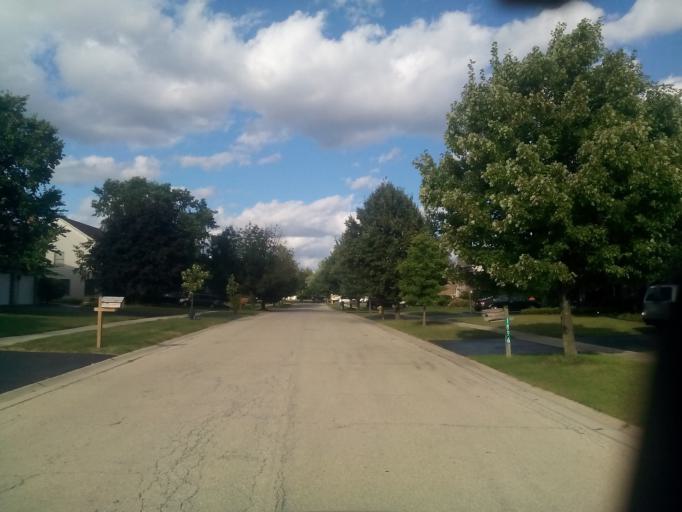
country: US
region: Illinois
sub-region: Will County
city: Romeoville
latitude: 41.6959
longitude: -88.1523
